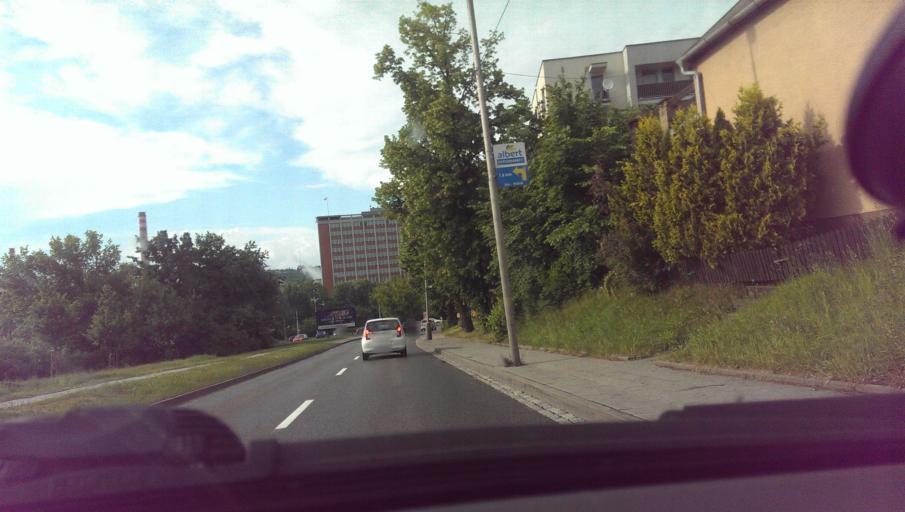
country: CZ
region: Zlin
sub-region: Okres Zlin
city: Zlin
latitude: 49.2198
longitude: 17.6598
